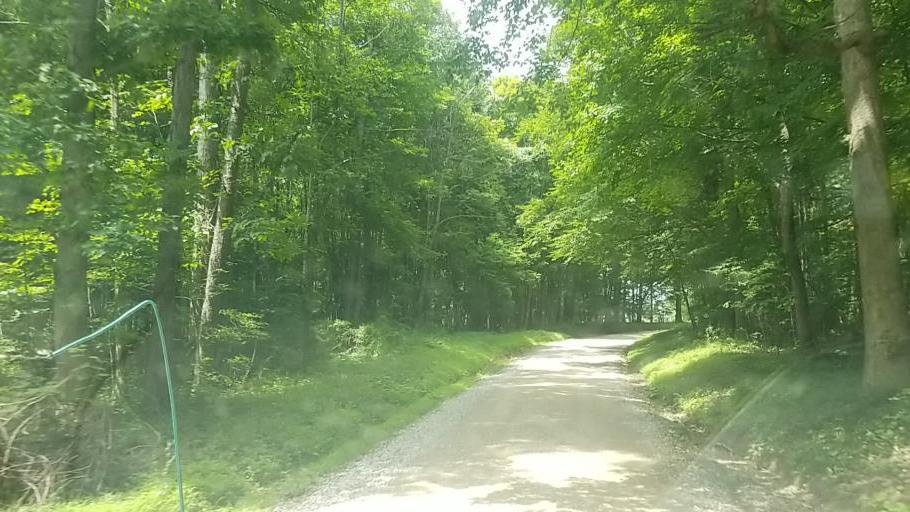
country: US
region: Ohio
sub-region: Licking County
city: Utica
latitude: 40.1806
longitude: -82.3242
